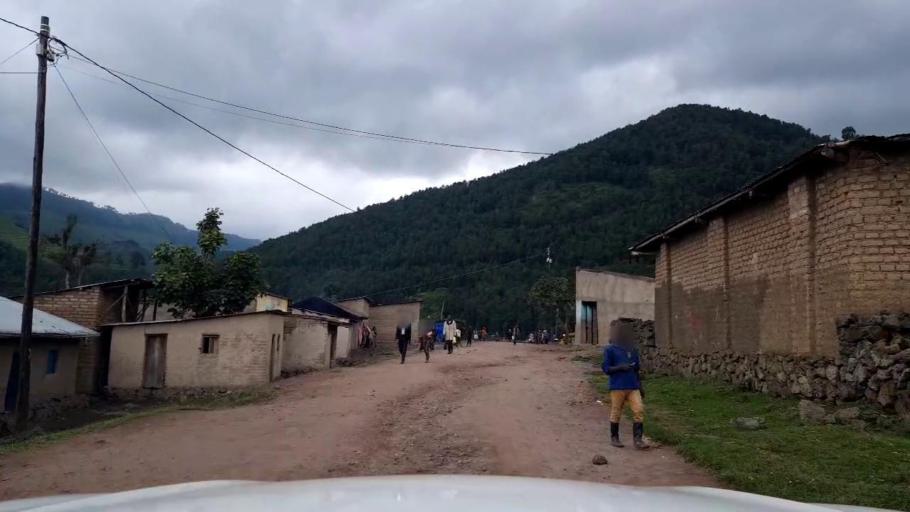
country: RW
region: Western Province
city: Gisenyi
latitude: -1.6439
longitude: 29.4099
